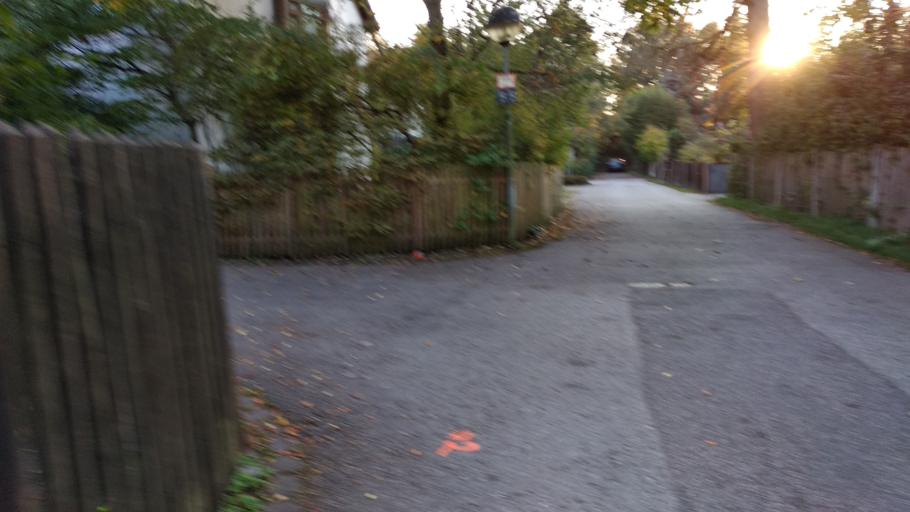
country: DE
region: Bavaria
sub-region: Upper Bavaria
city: Vaterstetten
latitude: 48.1052
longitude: 11.7633
